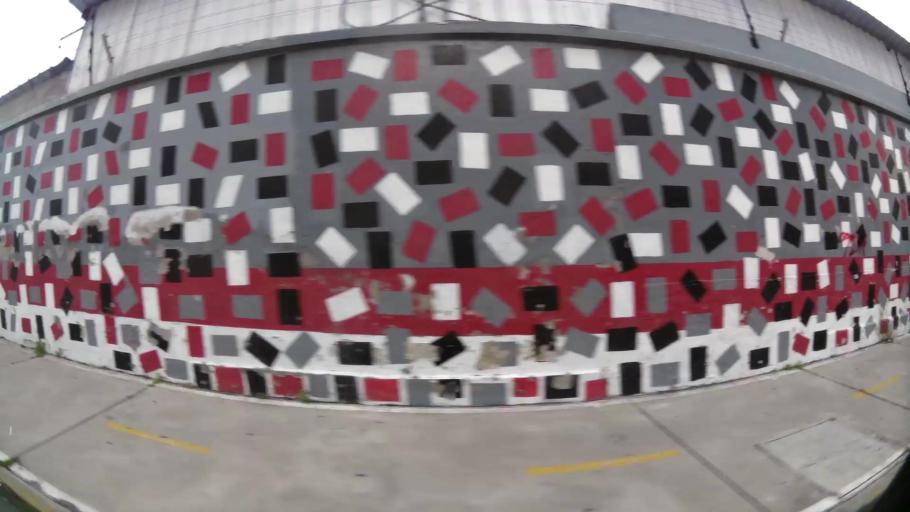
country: EC
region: Pichincha
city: Quito
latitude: -0.2024
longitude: -78.4970
